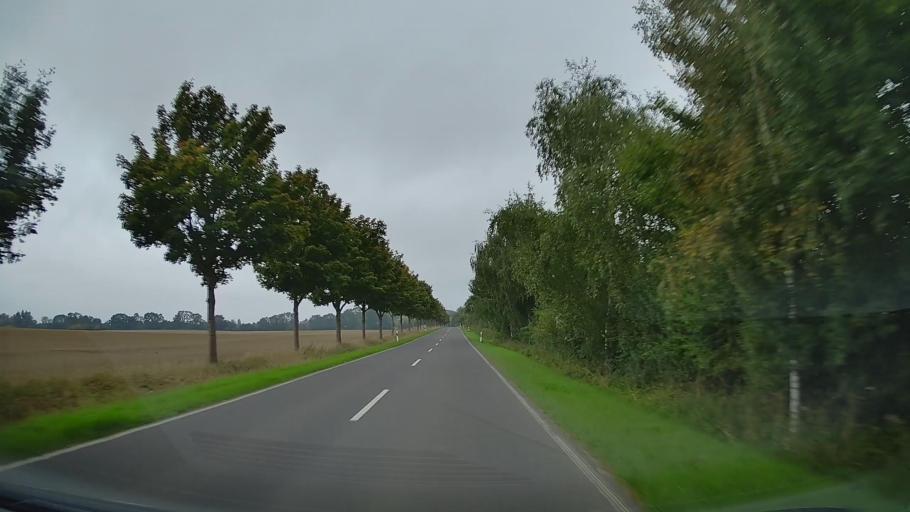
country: DE
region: Mecklenburg-Vorpommern
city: Tarnow
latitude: 53.7913
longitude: 12.0911
